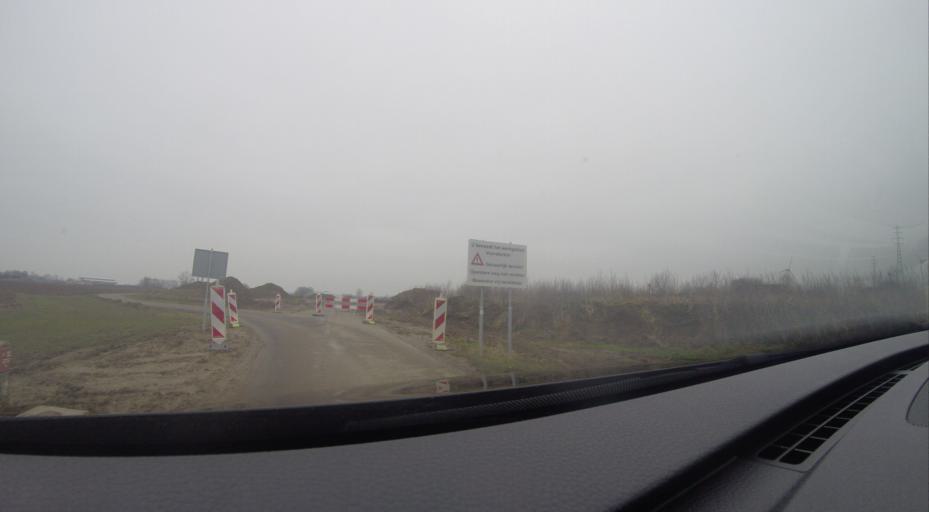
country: NL
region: Gelderland
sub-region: Gemeente Zutphen
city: Zutphen
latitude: 52.1619
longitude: 6.1763
